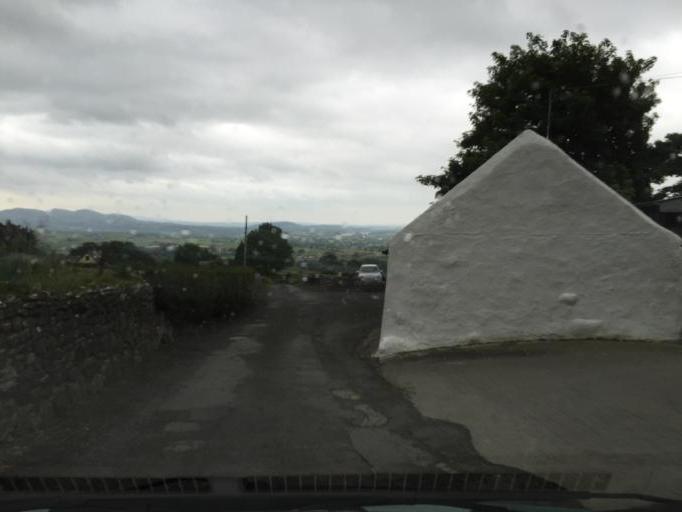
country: IE
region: Connaught
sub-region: Sligo
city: Strandhill
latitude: 54.2530
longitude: -8.5578
